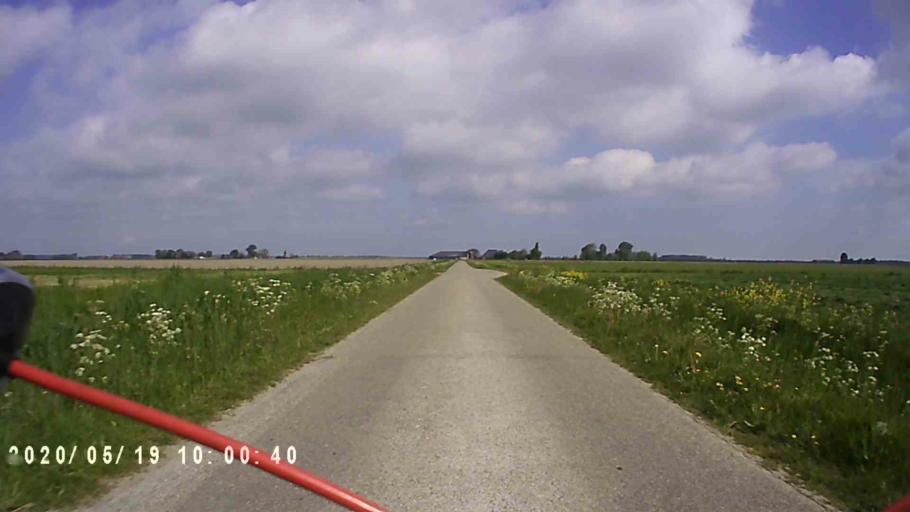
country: NL
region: Groningen
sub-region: Gemeente Zuidhorn
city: Grijpskerk
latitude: 53.2995
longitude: 6.2369
